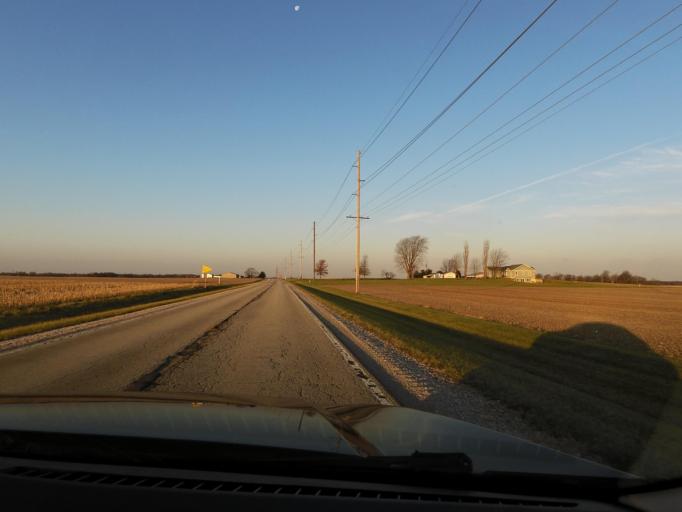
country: US
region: Illinois
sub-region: Marion County
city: Odin
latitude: 38.7651
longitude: -89.0263
